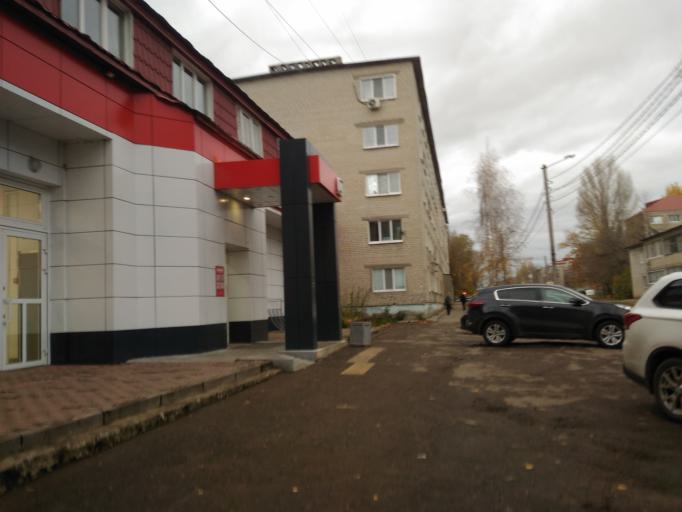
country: RU
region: Ulyanovsk
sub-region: Ulyanovskiy Rayon
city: Ulyanovsk
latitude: 54.3419
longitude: 48.3905
